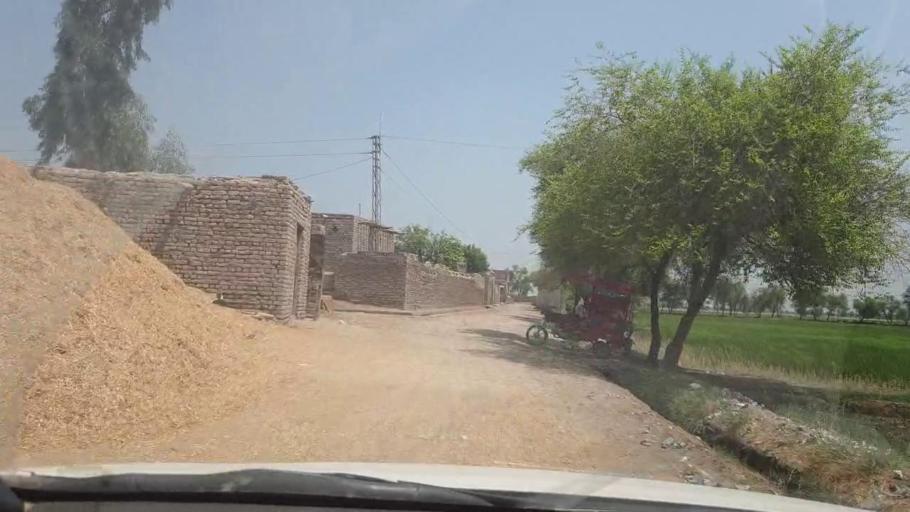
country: PK
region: Sindh
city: Lakhi
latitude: 27.8796
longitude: 68.7272
